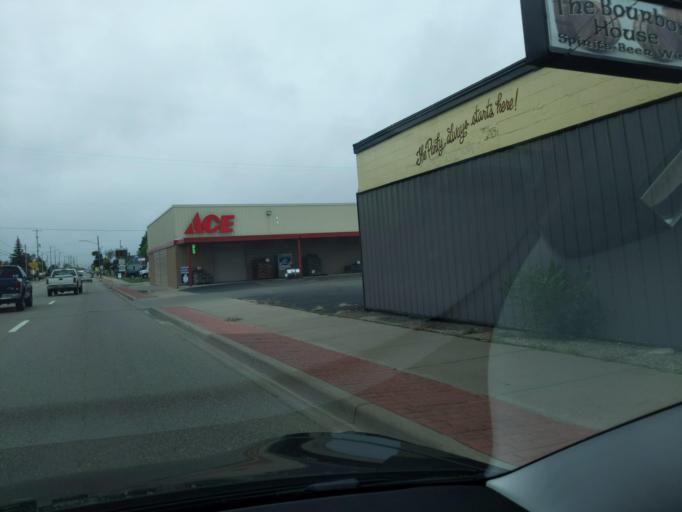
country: US
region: Michigan
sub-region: Wexford County
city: Cadillac
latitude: 44.2580
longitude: -85.4048
